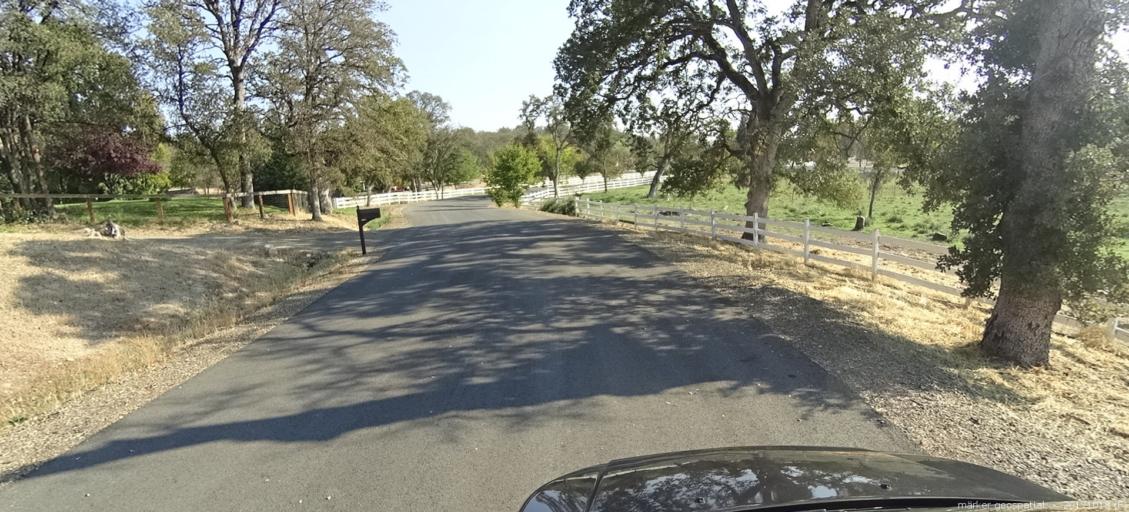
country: US
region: California
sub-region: Shasta County
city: Palo Cedro
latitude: 40.5761
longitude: -122.2518
